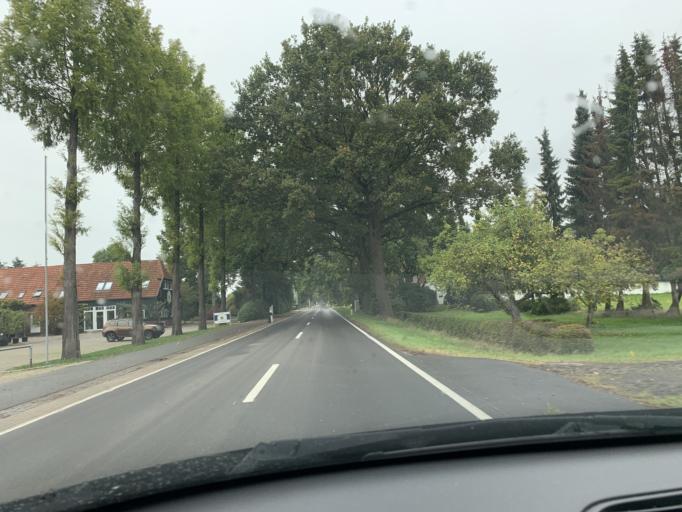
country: DE
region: Lower Saxony
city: Bad Zwischenahn
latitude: 53.1584
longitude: 8.0853
